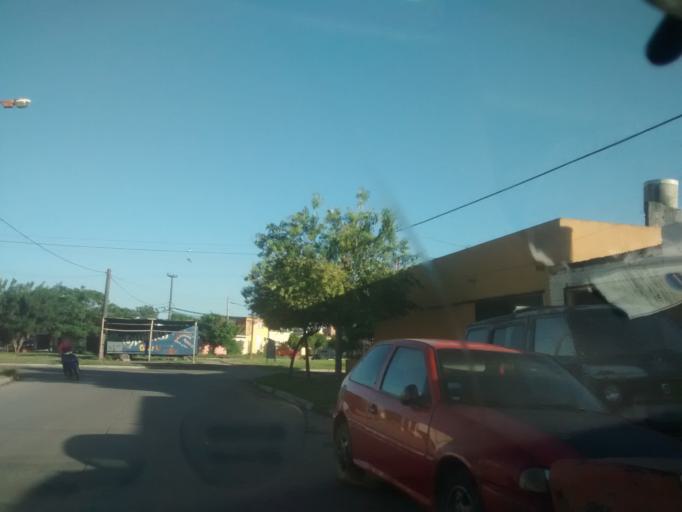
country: AR
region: Chaco
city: Resistencia
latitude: -27.4566
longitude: -59.0152
